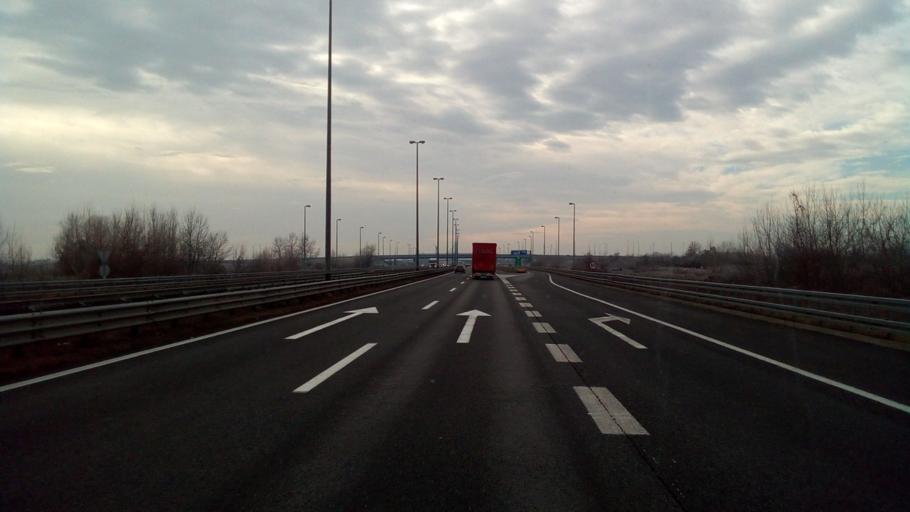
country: HR
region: Zagrebacka
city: Micevec
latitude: 45.7686
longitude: 16.0955
